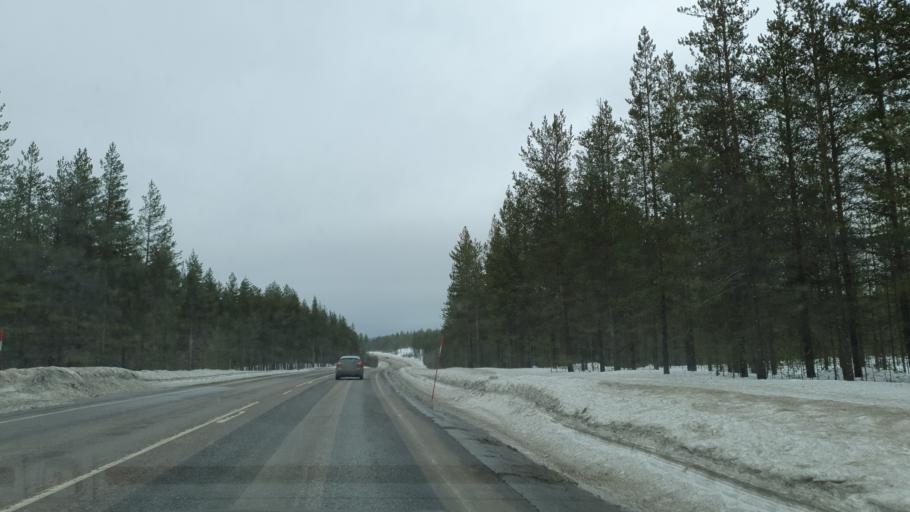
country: FI
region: Lapland
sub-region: Torniolaakso
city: Pello
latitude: 66.9240
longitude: 24.0866
